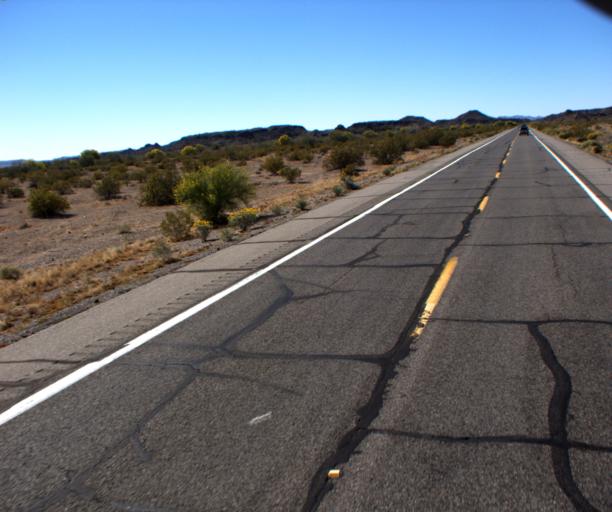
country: US
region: Arizona
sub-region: Pima County
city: Ajo
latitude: 32.5793
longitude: -112.8741
